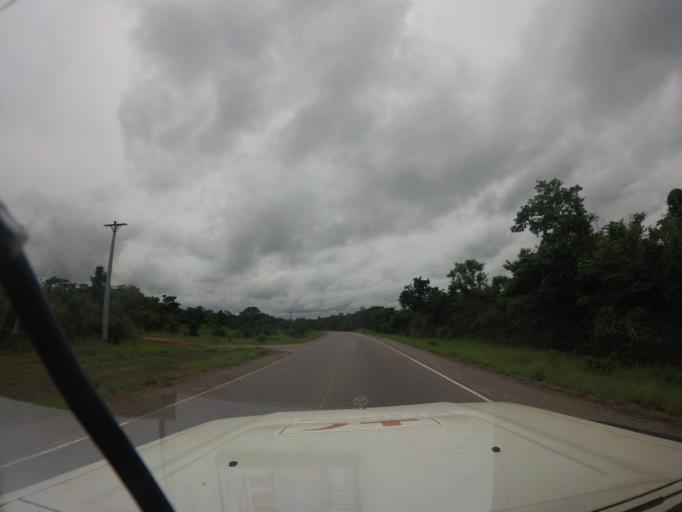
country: SL
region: Northern Province
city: Magburaka
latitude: 8.7483
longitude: -11.9640
